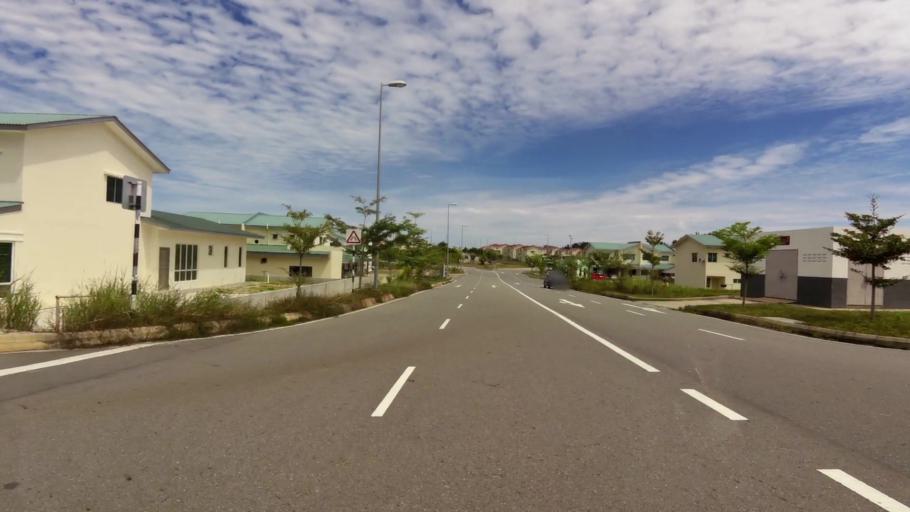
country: BN
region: Brunei and Muara
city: Bandar Seri Begawan
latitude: 4.9716
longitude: 115.0083
